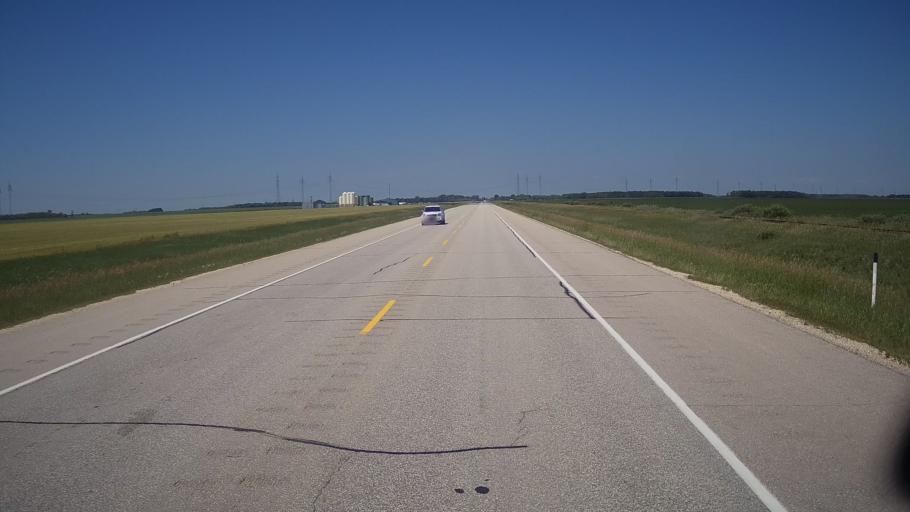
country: CA
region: Manitoba
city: Stonewall
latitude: 50.0460
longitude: -97.4142
